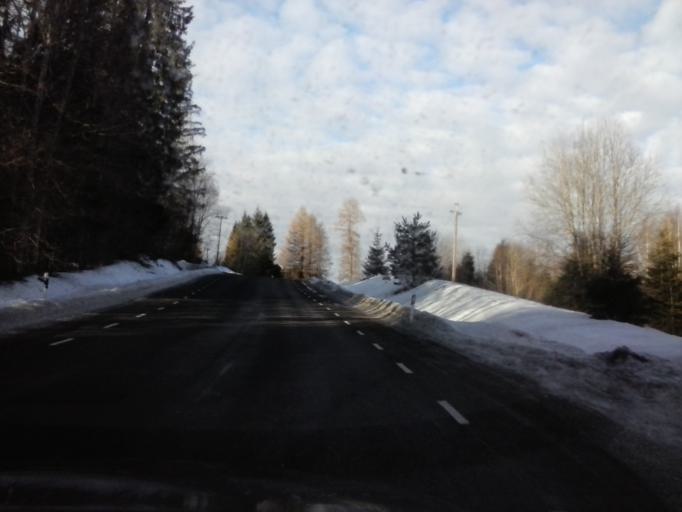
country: EE
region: Tartu
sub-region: Elva linn
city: Elva
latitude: 58.0431
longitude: 26.3914
